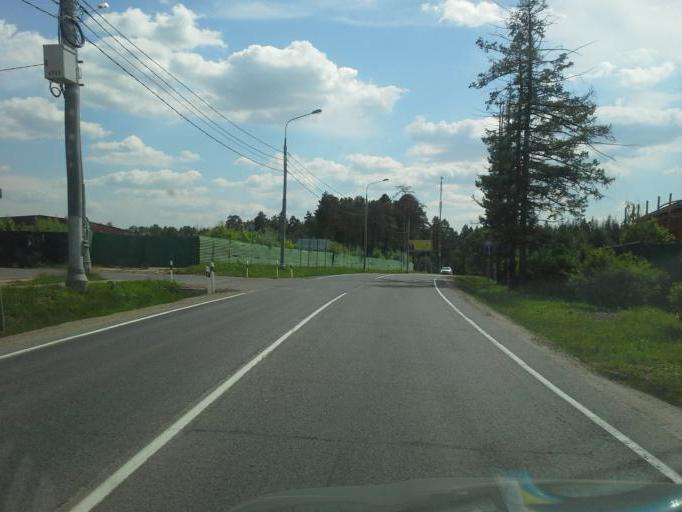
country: RU
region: Moskovskaya
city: Odintsovo
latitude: 55.7102
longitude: 37.2710
